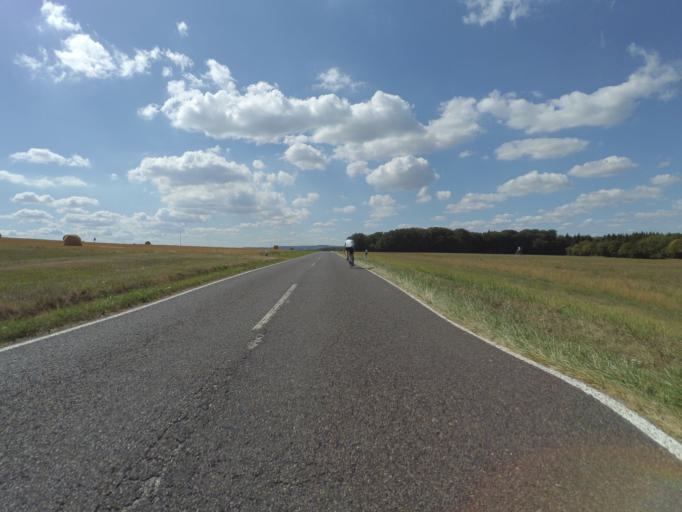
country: LU
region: Grevenmacher
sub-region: Canton de Grevenmacher
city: Wormeldange
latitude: 49.5740
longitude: 6.4013
